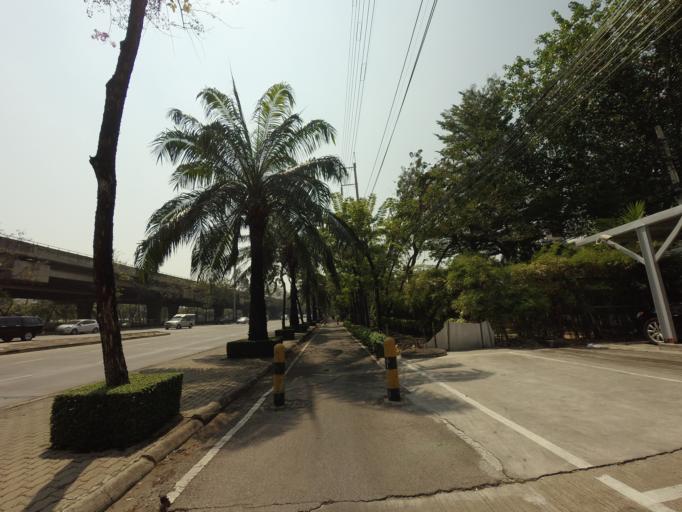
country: TH
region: Bangkok
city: Wang Thonglang
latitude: 13.7834
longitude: 100.6075
